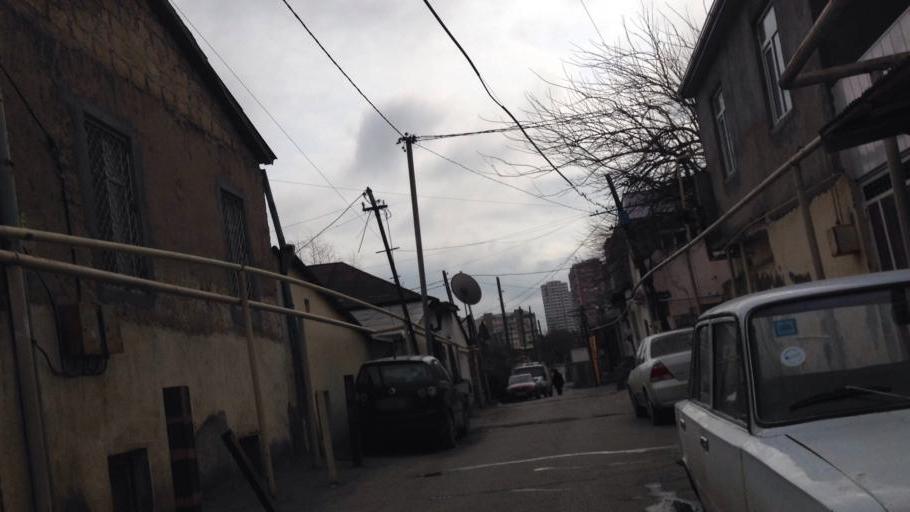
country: AZ
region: Baki
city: Bilajari
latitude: 40.4001
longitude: 49.8280
